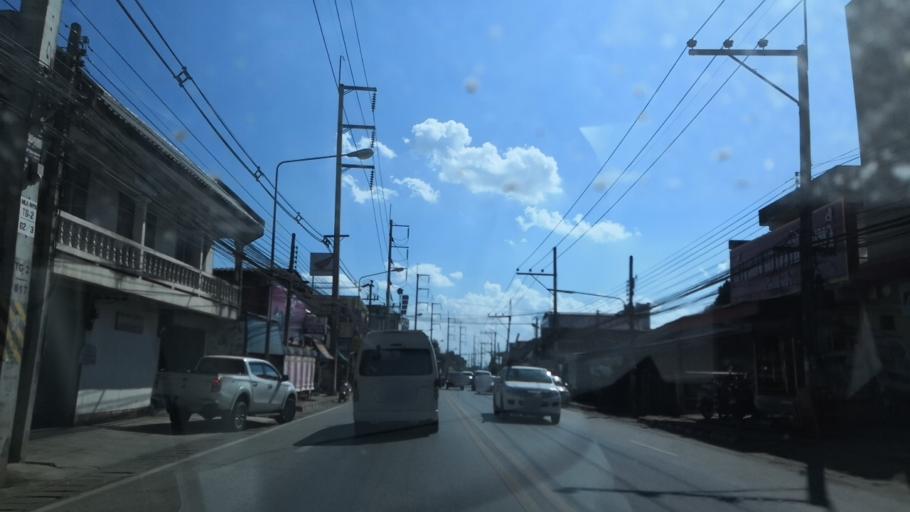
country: TH
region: Chiang Rai
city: Wiang Pa Pao
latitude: 19.3671
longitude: 99.5035
